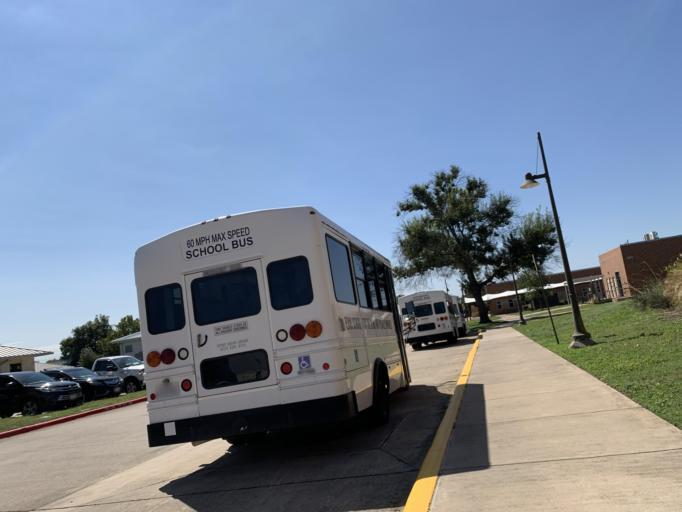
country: US
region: Texas
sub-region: Travis County
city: Austin
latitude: 30.3162
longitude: -97.7375
